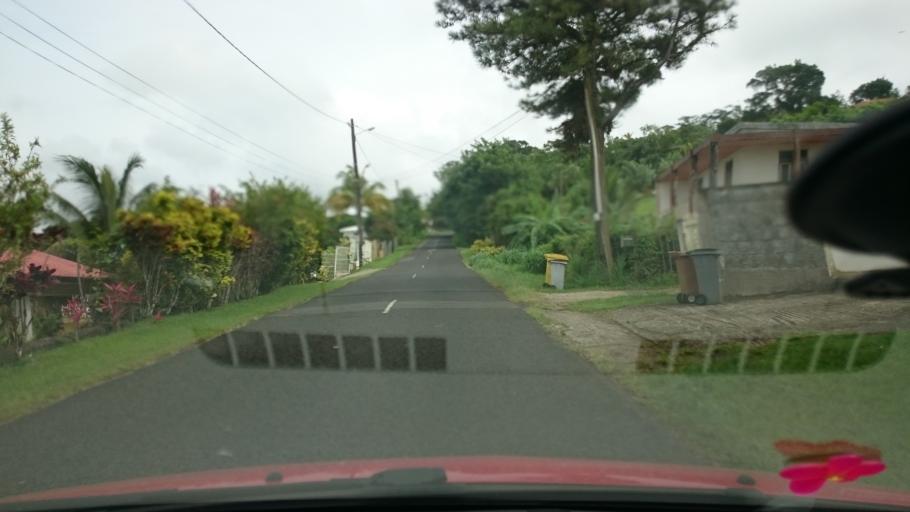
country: MQ
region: Martinique
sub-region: Martinique
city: Sainte-Luce
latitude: 14.4959
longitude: -60.9258
